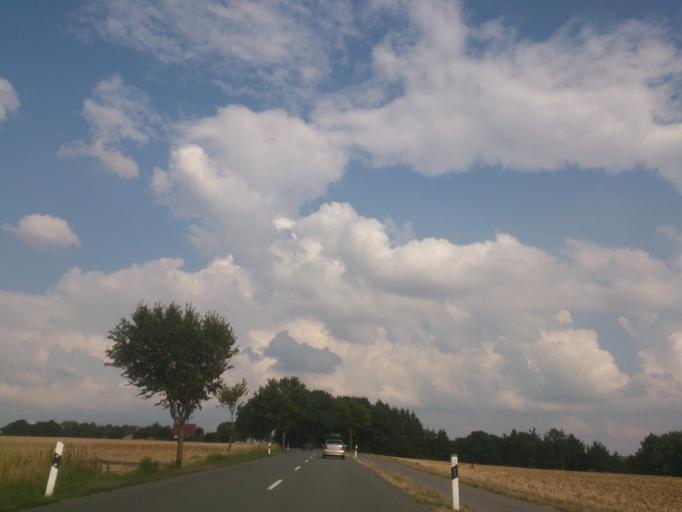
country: DE
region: North Rhine-Westphalia
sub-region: Regierungsbezirk Detmold
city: Paderborn
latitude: 51.6988
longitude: 8.8237
